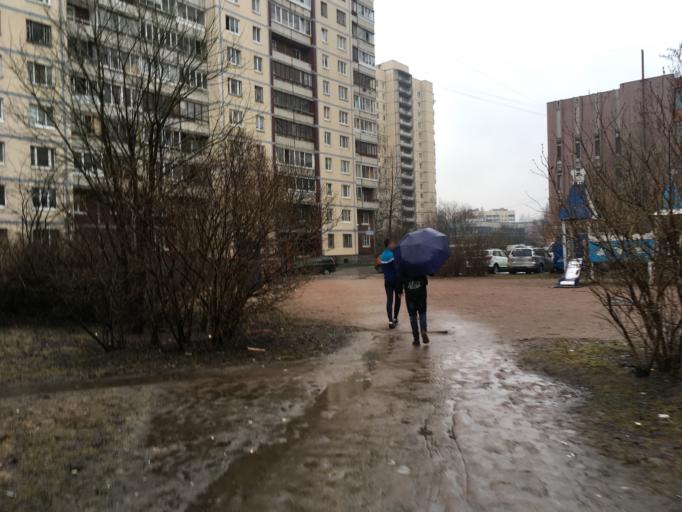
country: RU
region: St.-Petersburg
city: Komendantsky aerodrom
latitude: 60.0137
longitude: 30.2550
